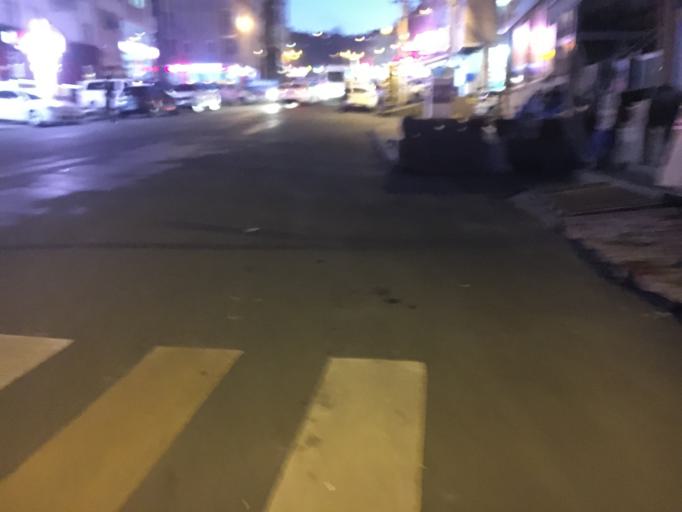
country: TR
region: Trabzon
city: Trabzon
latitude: 40.9927
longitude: 39.7798
